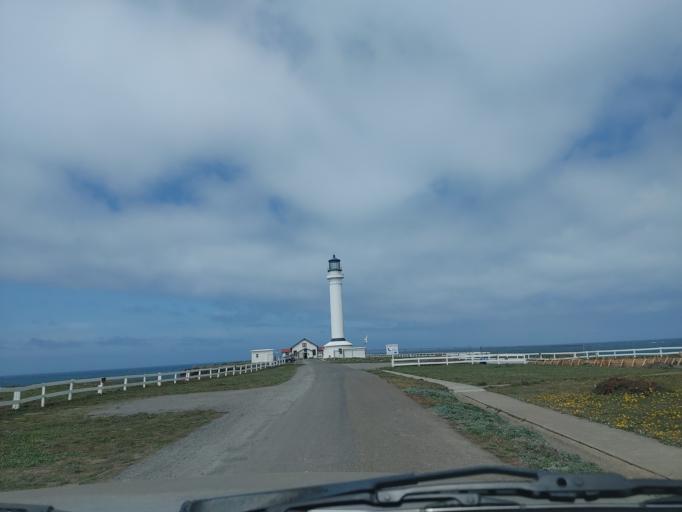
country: US
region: California
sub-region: Sonoma County
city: Sea Ranch
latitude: 38.9537
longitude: -123.7392
